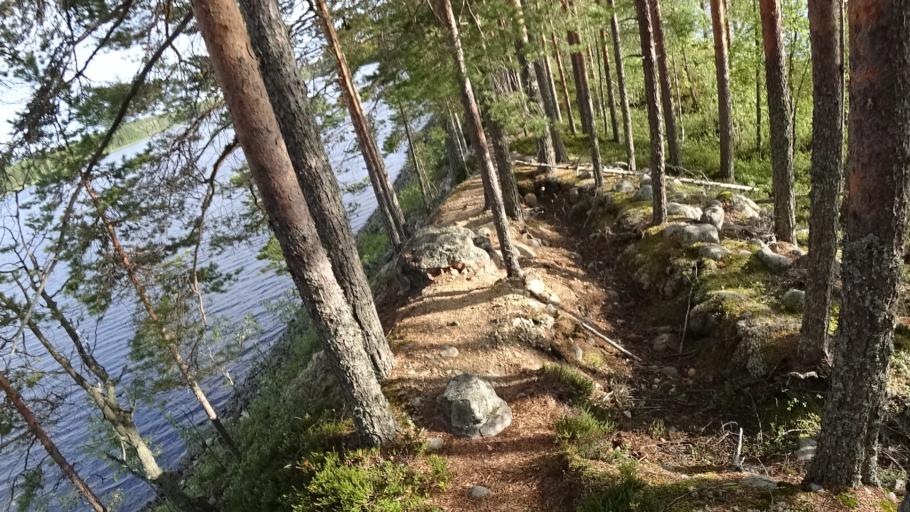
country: FI
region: North Karelia
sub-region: Joensuu
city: Ilomantsi
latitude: 62.5663
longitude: 31.1827
